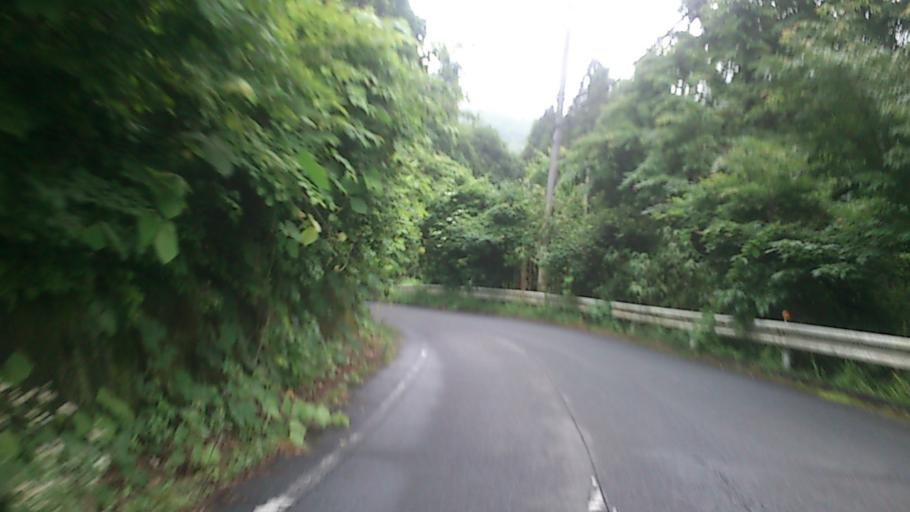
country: JP
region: Ibaraki
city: Omiya
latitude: 36.6220
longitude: 140.3613
